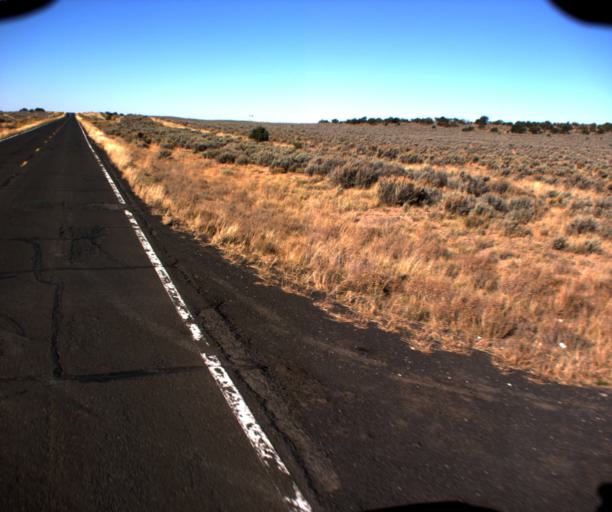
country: US
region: Arizona
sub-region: Navajo County
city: First Mesa
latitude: 35.7559
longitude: -110.0240
